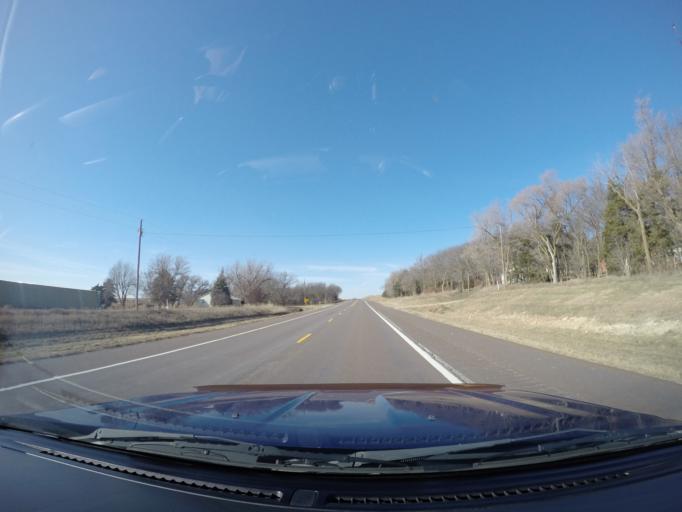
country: US
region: Kansas
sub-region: Clay County
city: Clay Center
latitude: 39.3795
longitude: -96.9733
